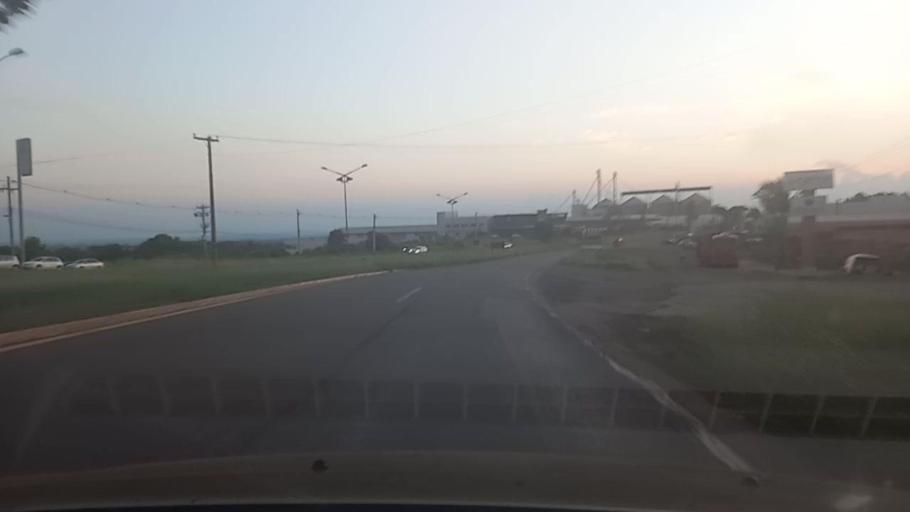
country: BR
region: Rio Grande do Sul
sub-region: Passo Fundo
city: Passo Fundo
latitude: -28.2709
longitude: -52.4413
